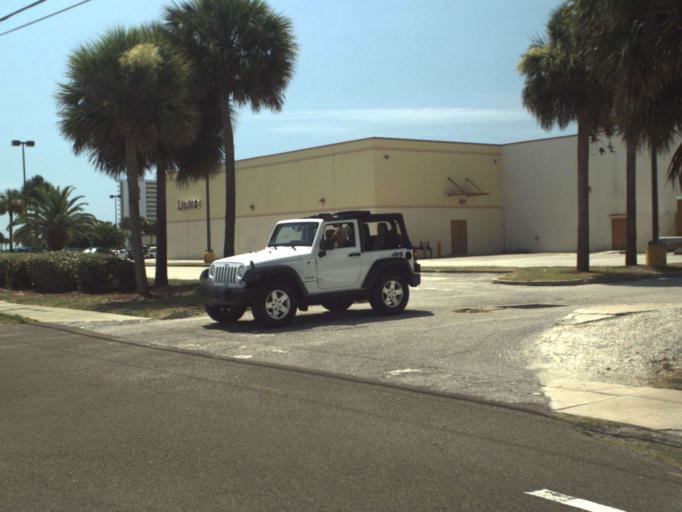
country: US
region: Florida
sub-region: Brevard County
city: Indian Harbour Beach
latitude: 28.1386
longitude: -80.5850
